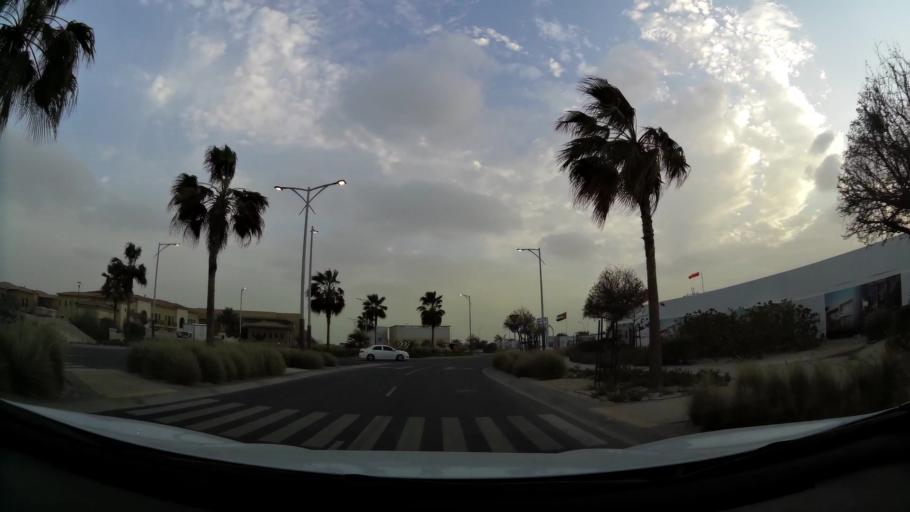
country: AE
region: Abu Dhabi
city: Abu Dhabi
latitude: 24.5351
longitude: 54.4277
